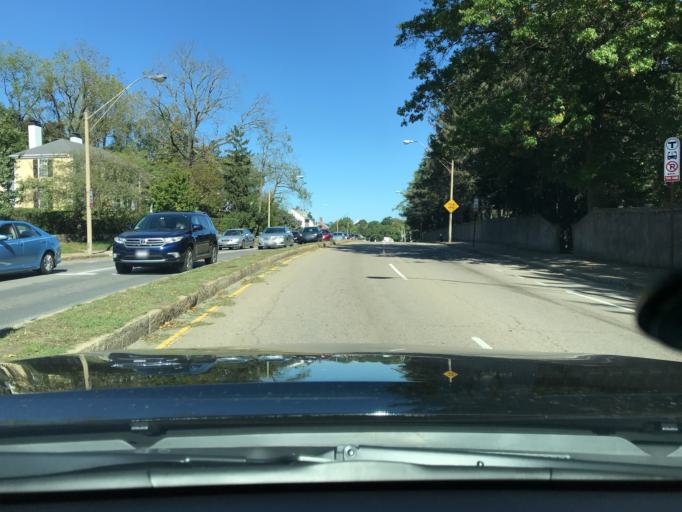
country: US
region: Massachusetts
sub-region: Suffolk County
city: Jamaica Plain
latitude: 42.3061
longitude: -71.1242
